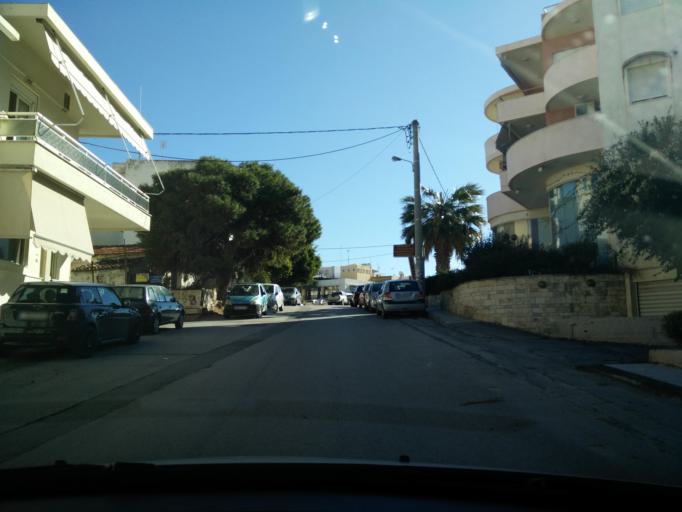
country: GR
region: Crete
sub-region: Nomos Irakleiou
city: Irakleion
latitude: 35.3284
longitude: 25.1425
